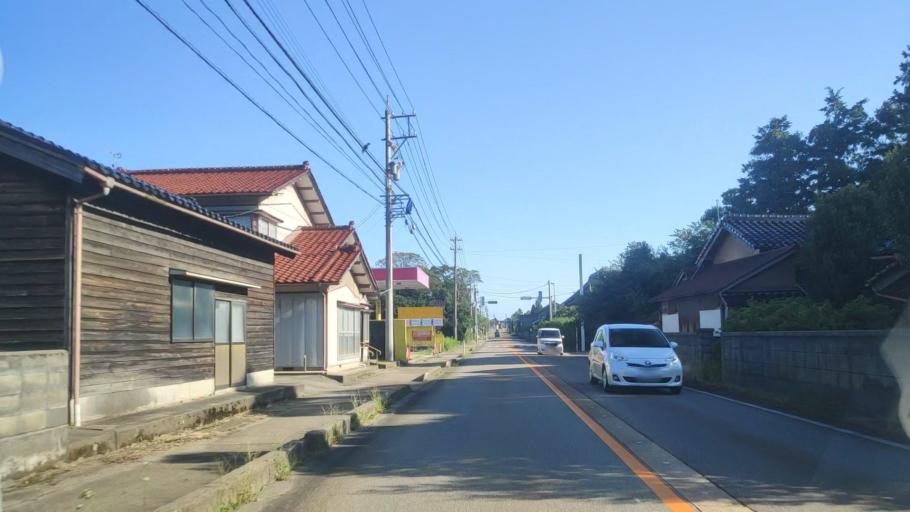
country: JP
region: Ishikawa
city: Hakui
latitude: 36.8384
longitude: 136.7630
